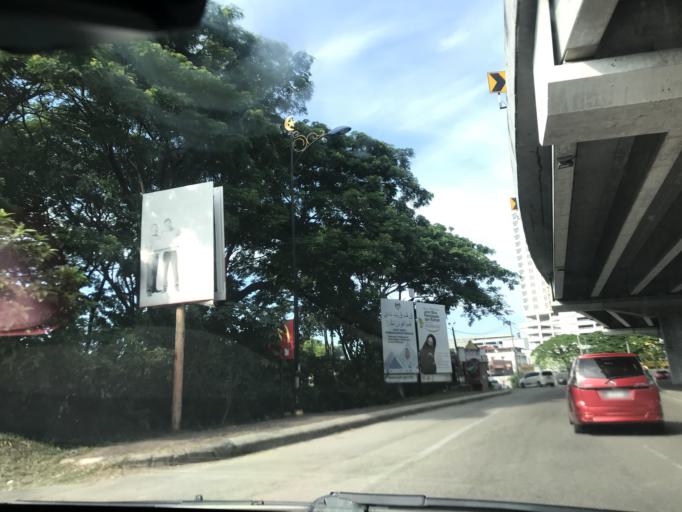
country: MY
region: Kelantan
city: Kota Bharu
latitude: 6.1167
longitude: 102.2371
